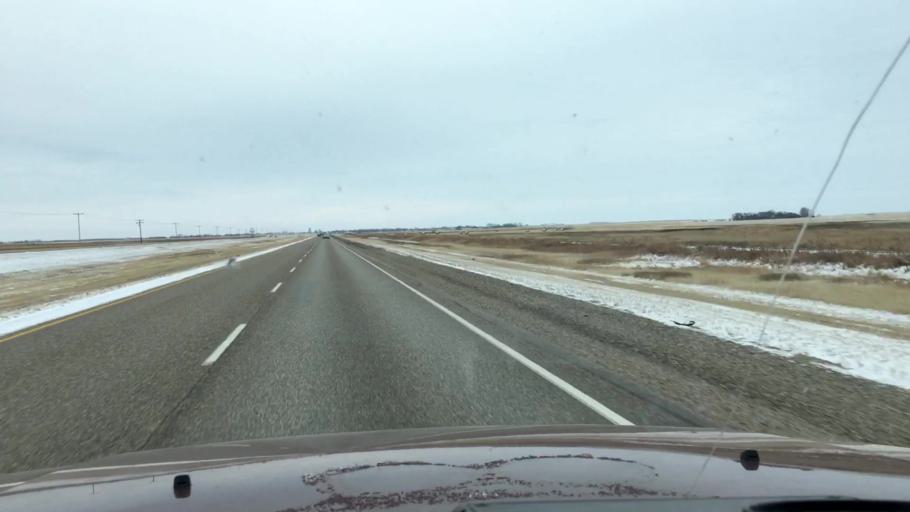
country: CA
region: Saskatchewan
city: Watrous
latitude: 51.0850
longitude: -105.8528
